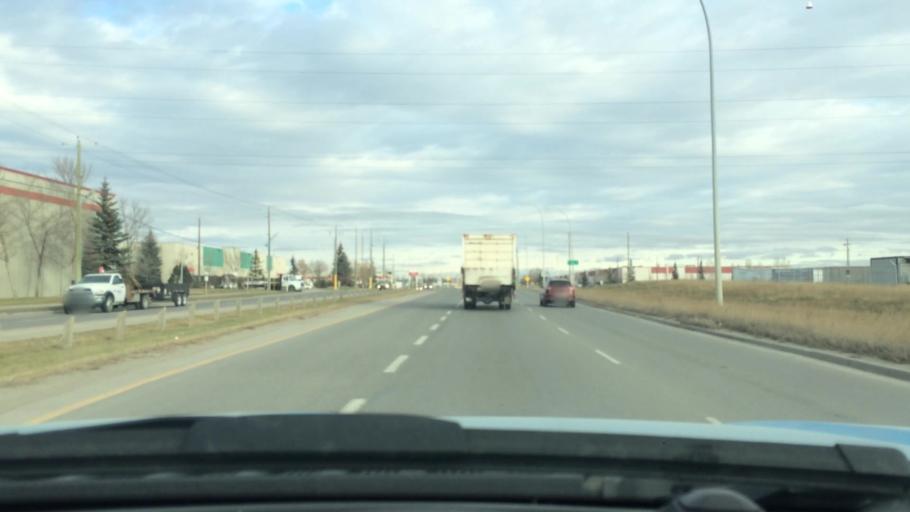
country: CA
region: Alberta
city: Calgary
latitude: 51.0057
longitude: -113.9584
